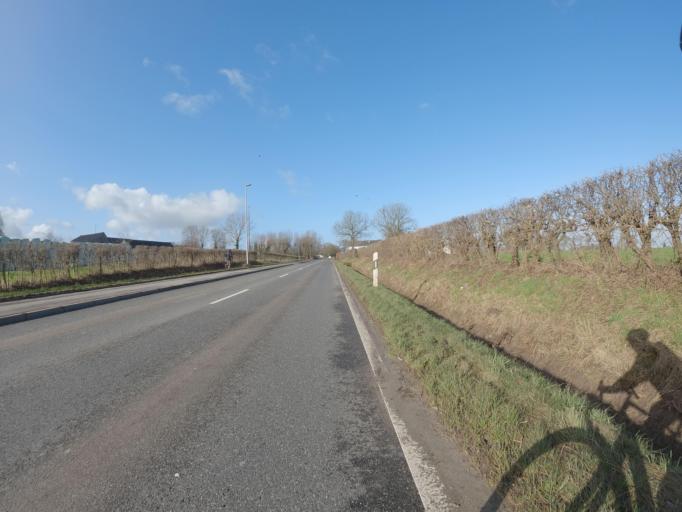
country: BE
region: Wallonia
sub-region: Province de Liege
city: Raeren
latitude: 50.7175
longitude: 6.1640
